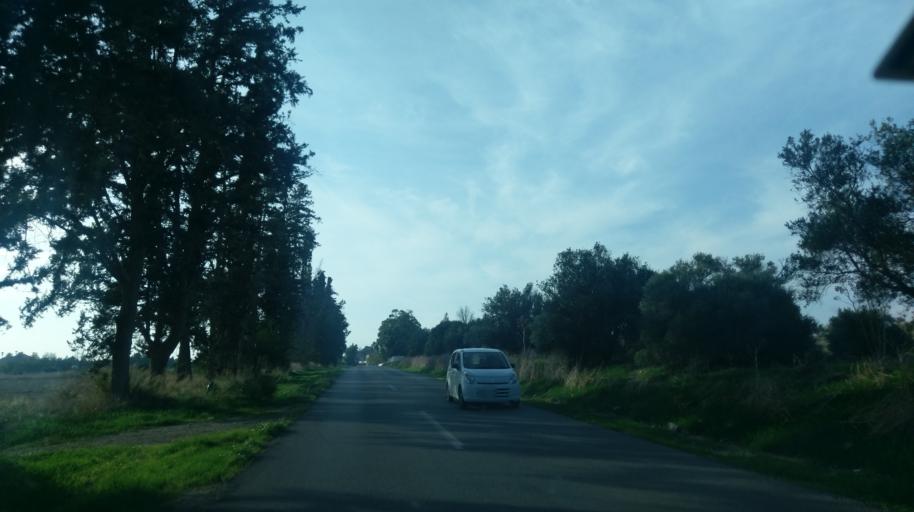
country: CY
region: Ammochostos
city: Achna
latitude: 35.1073
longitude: 33.7569
